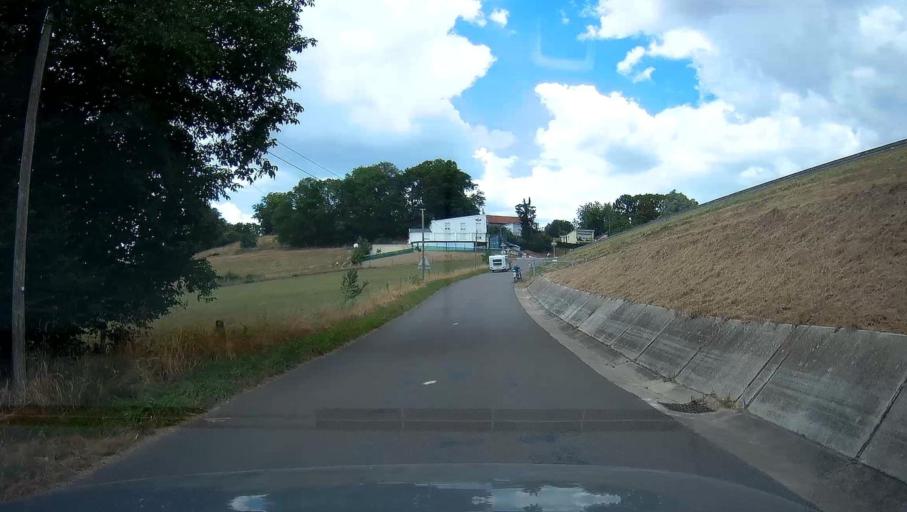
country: FR
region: Champagne-Ardenne
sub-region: Departement de la Haute-Marne
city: Langres
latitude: 47.8672
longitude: 5.3725
